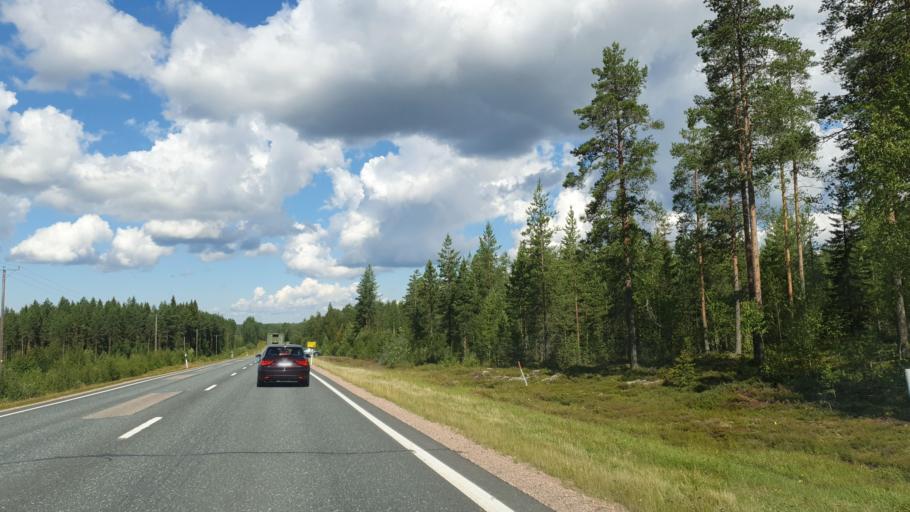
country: FI
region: Kainuu
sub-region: Kajaani
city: Kajaani
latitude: 64.0994
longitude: 27.4496
